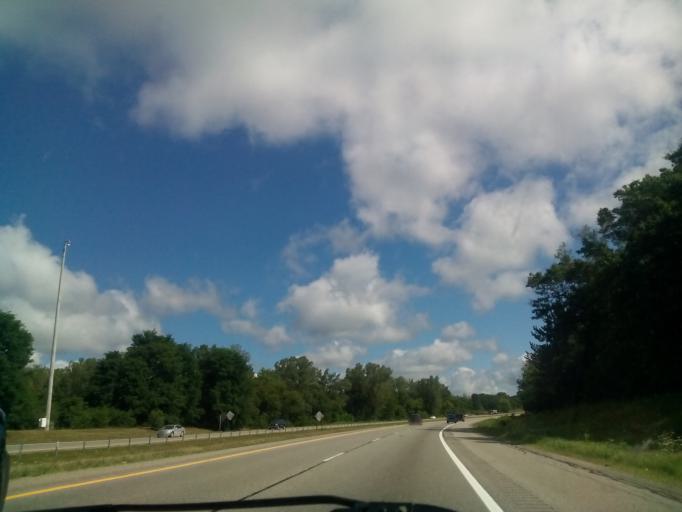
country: US
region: Michigan
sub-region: Livingston County
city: Brighton
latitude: 42.5501
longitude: -83.7488
